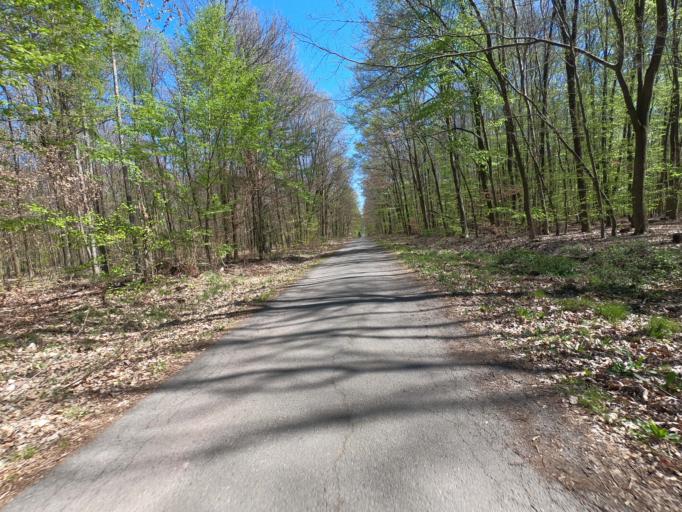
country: DE
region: Hesse
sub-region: Regierungsbezirk Darmstadt
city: Messel
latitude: 49.9302
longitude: 8.7184
